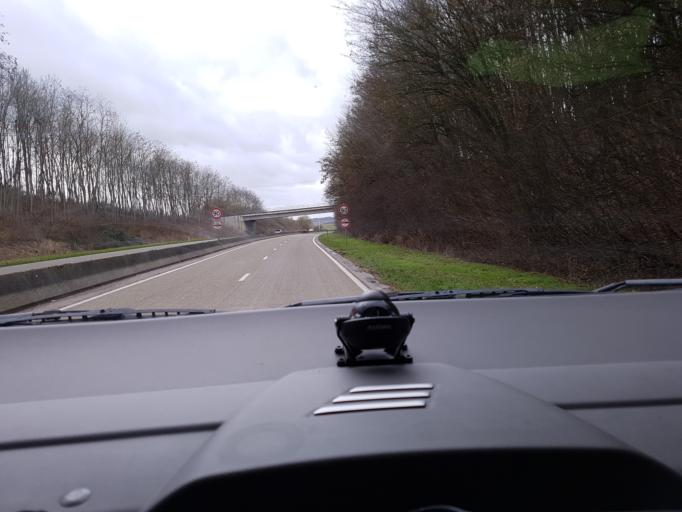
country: BE
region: Wallonia
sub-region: Province de Namur
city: Onhaye
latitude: 50.2439
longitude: 4.8308
